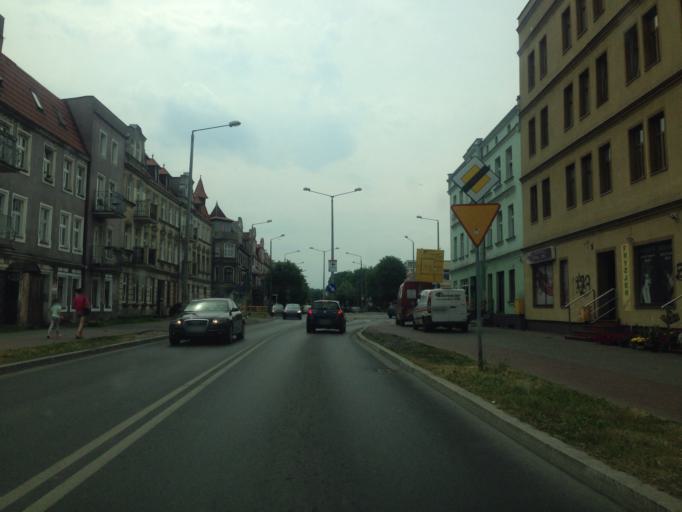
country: PL
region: Kujawsko-Pomorskie
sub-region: Grudziadz
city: Grudziadz
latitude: 53.5012
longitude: 18.7774
